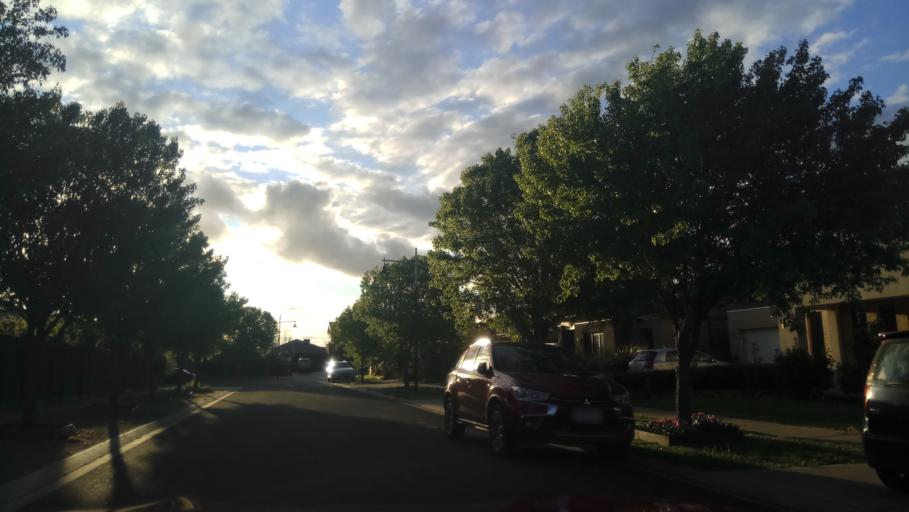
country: AU
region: Victoria
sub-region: Wyndham
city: Point Cook
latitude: -37.9056
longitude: 144.7391
